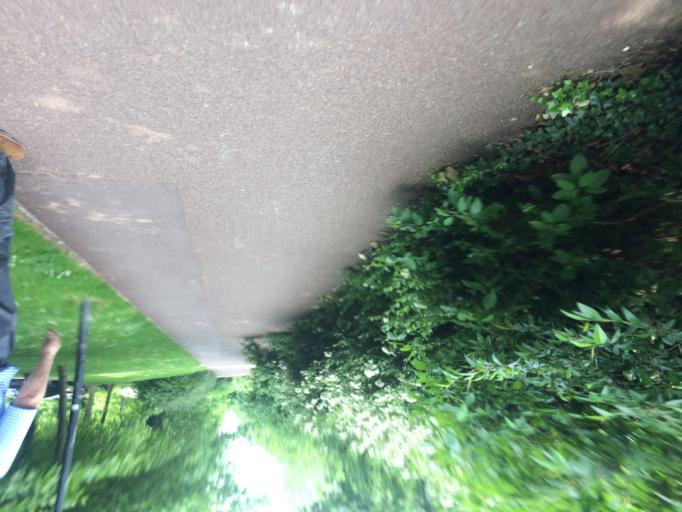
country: GB
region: England
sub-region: Milton Keynes
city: Loughton
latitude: 52.0387
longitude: -0.7752
